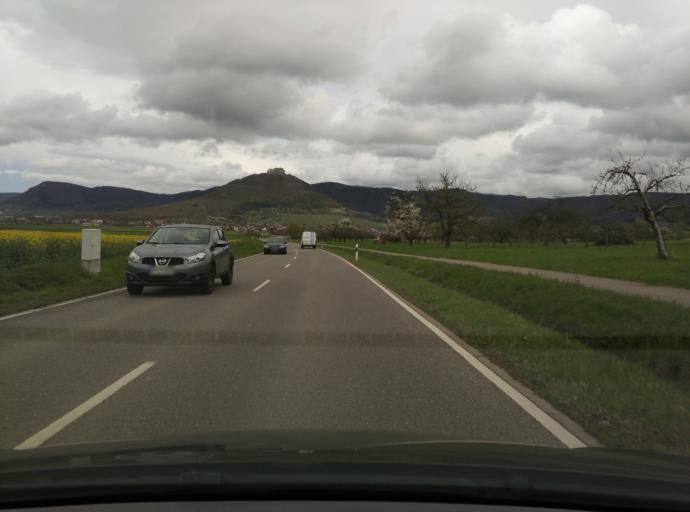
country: DE
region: Baden-Wuerttemberg
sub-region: Regierungsbezirk Stuttgart
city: Kohlberg
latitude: 48.5575
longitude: 9.3506
